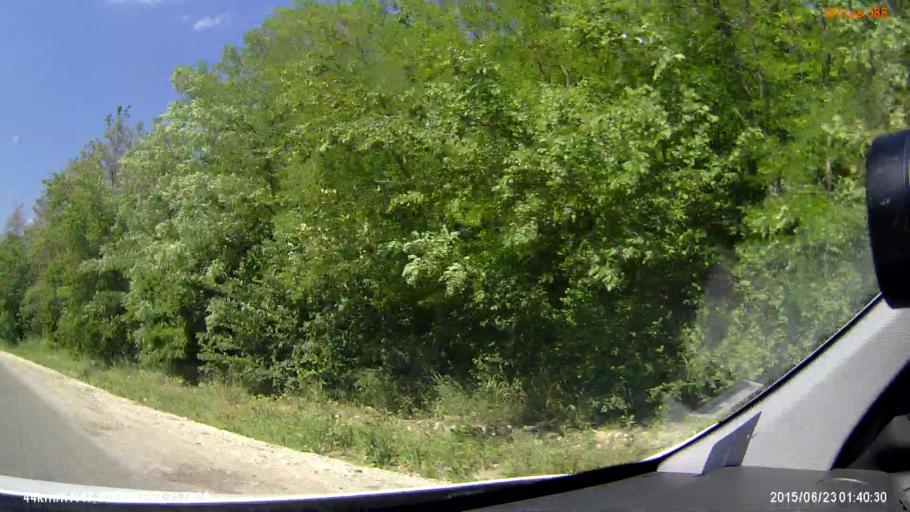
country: RO
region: Iasi
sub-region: Comuna Golaesti
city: Golaesti
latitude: 47.3088
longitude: 27.7171
